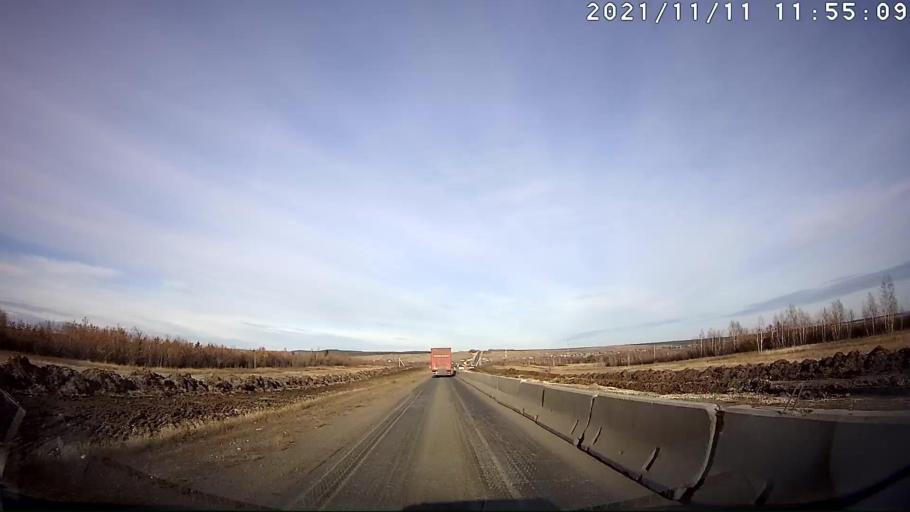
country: RU
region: Samara
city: Balasheyka
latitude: 53.5370
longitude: 48.3373
